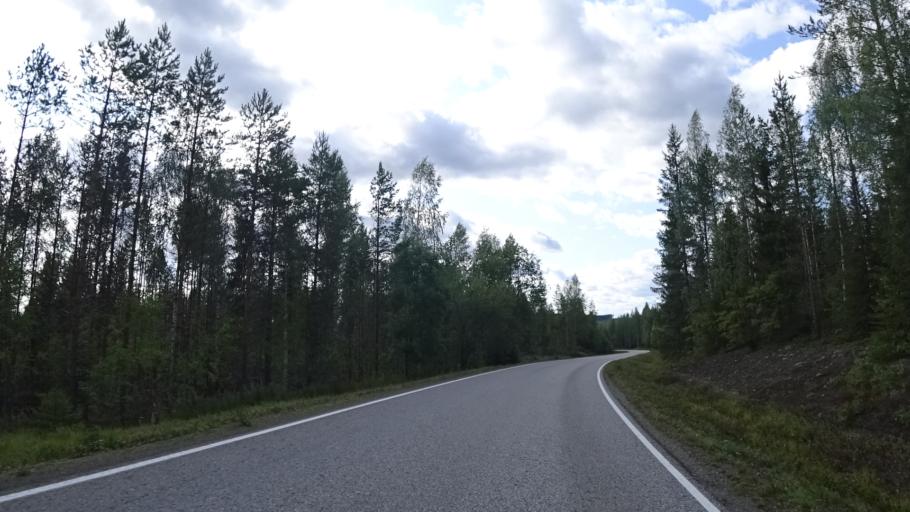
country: RU
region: Republic of Karelia
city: Vyartsilya
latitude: 62.2220
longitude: 30.6418
